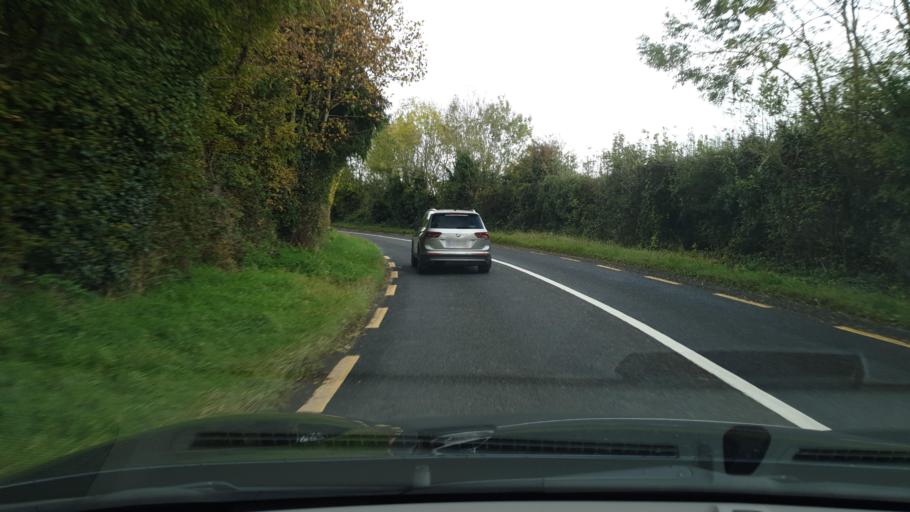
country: IE
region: Leinster
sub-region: An Mhi
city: Dunshaughlin
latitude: 53.5189
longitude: -6.5312
